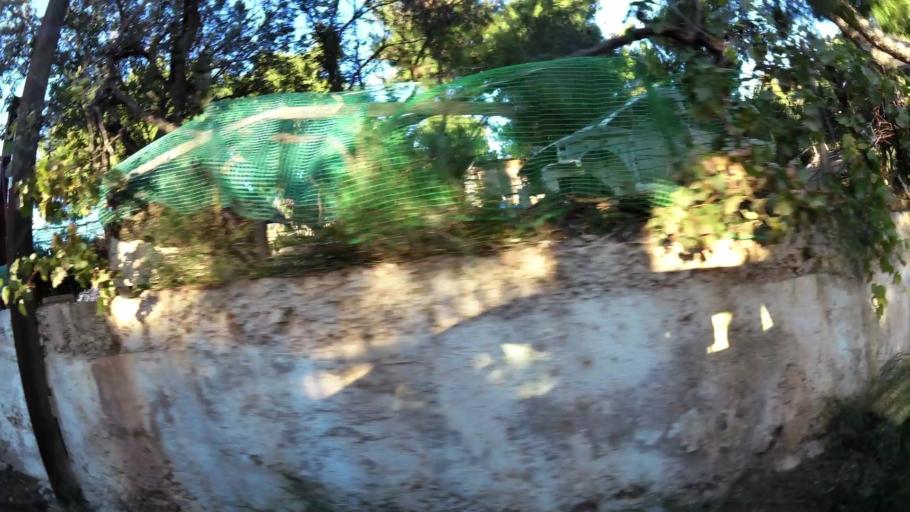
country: GR
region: Attica
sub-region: Nomarchia Athinas
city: Penteli
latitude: 38.0438
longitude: 23.8603
